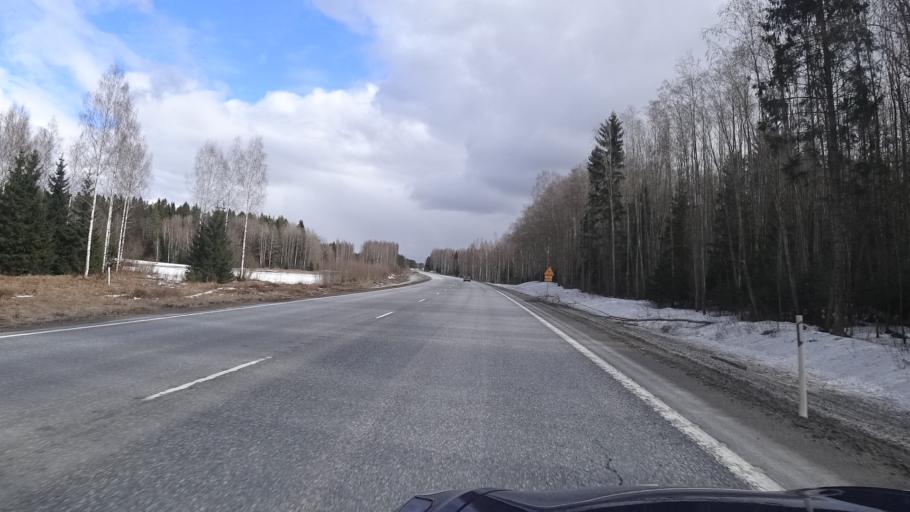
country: FI
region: Paijanne Tavastia
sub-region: Lahti
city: Lahti
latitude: 60.9534
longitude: 25.7871
